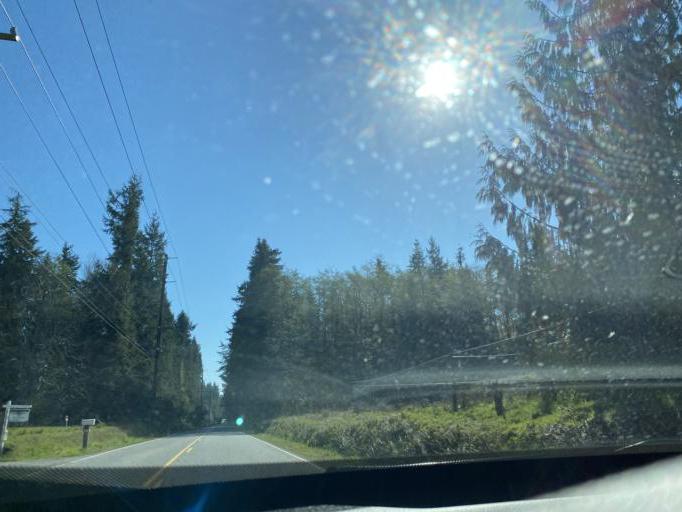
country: US
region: Washington
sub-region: Island County
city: Freeland
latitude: 48.0798
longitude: -122.5951
